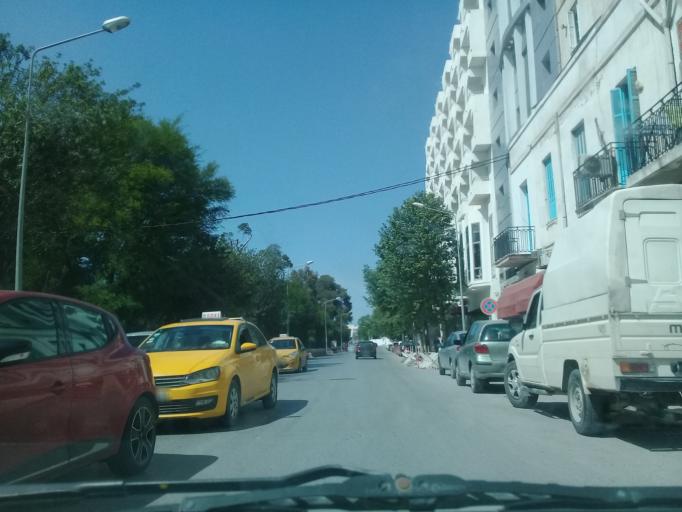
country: TN
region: Tunis
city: Tunis
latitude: 36.8168
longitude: 10.1764
